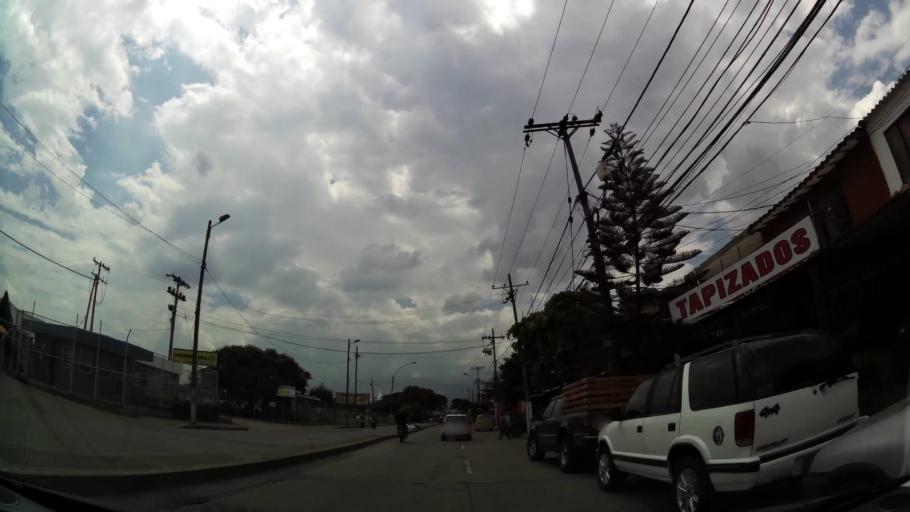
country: CO
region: Valle del Cauca
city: Cali
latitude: 3.4653
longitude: -76.4922
